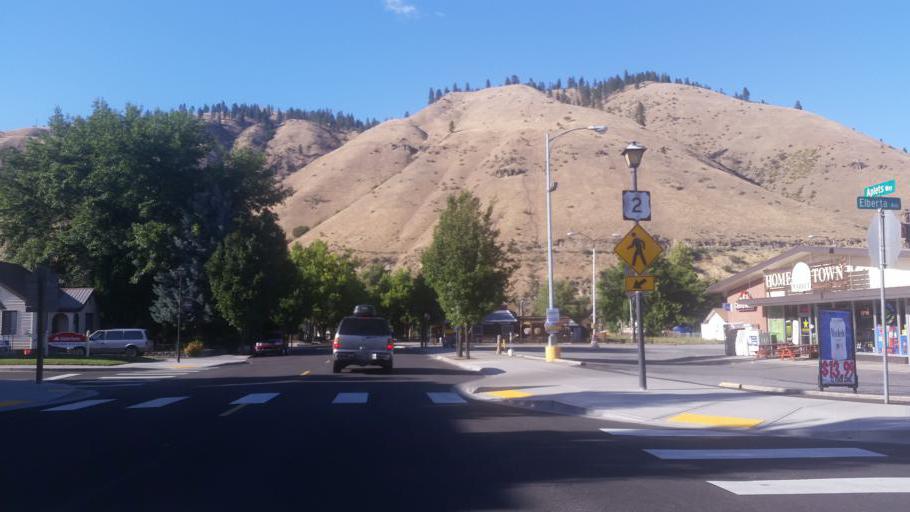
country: US
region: Washington
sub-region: Chelan County
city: Cashmere
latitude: 47.5228
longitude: -120.4700
